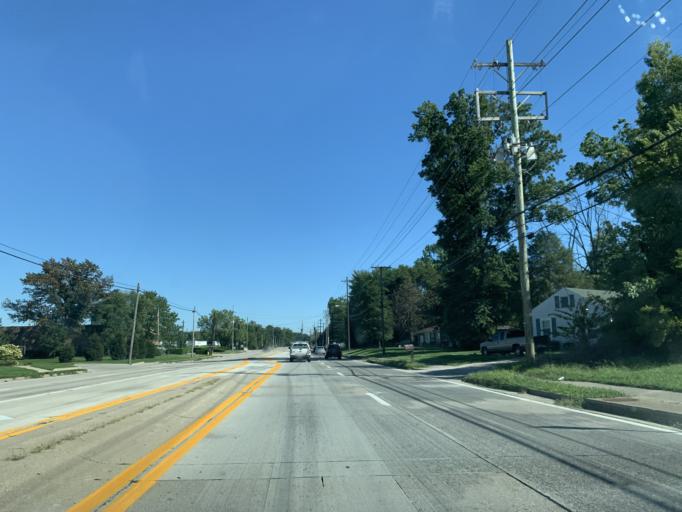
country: US
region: Kentucky
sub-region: Jefferson County
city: West Buechel
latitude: 38.1813
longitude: -85.6959
